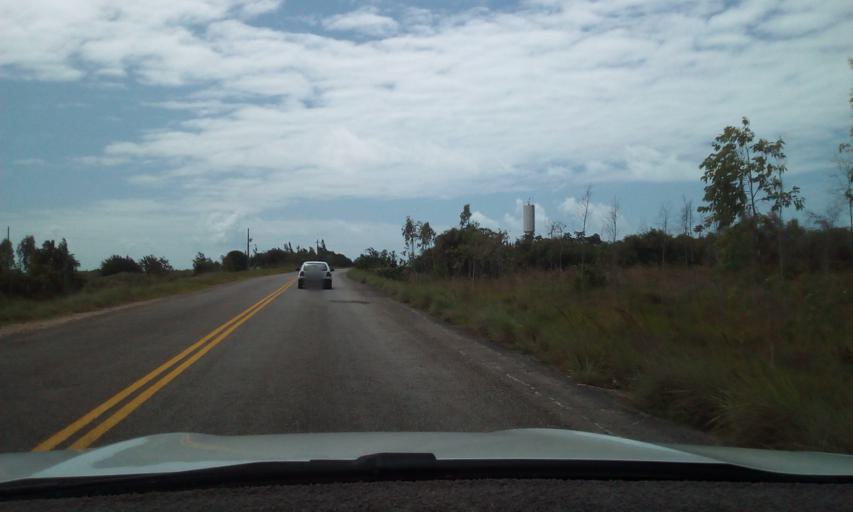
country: BR
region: Paraiba
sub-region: Rio Tinto
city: Rio Tinto
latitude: -6.7297
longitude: -34.9582
